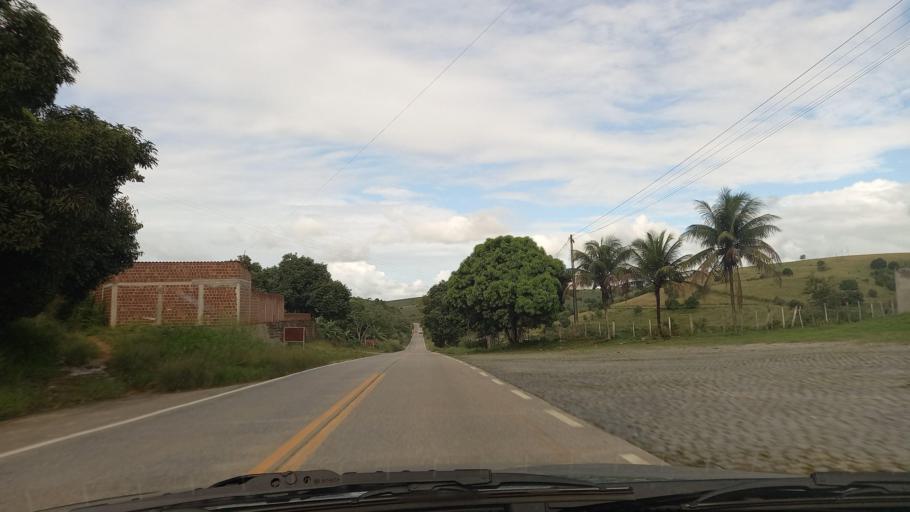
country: BR
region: Pernambuco
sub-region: Catende
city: Catende
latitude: -8.6918
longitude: -35.7208
